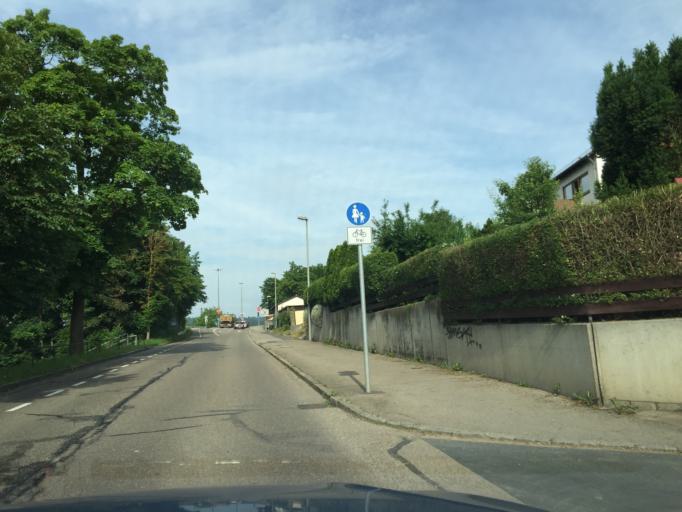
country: DE
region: Baden-Wuerttemberg
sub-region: Tuebingen Region
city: Ulm
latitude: 48.4031
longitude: 9.9584
